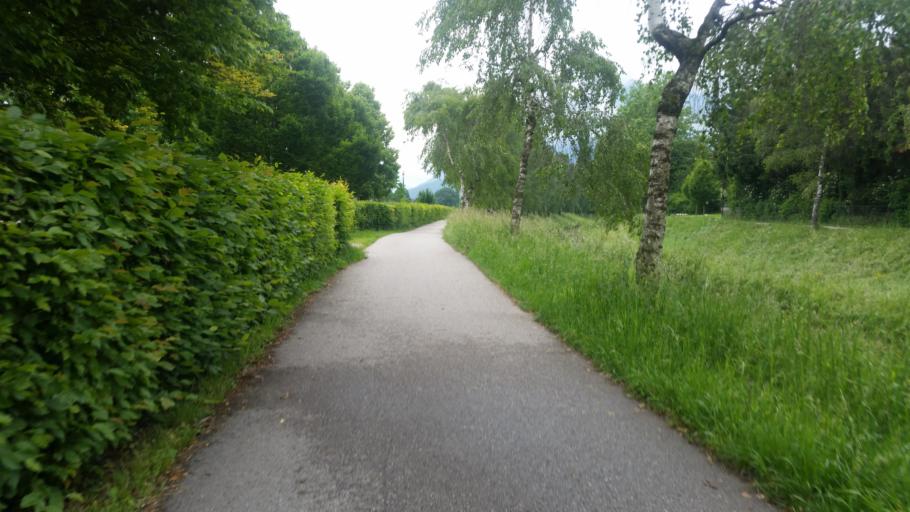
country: AT
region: Salzburg
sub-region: Salzburg Stadt
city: Salzburg
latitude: 47.7900
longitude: 13.0209
